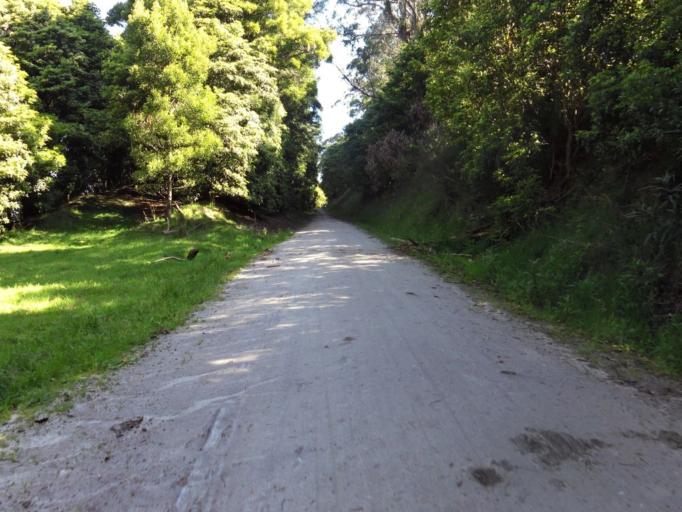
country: AU
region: Victoria
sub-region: Latrobe
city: Morwell
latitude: -38.6805
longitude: 146.1579
